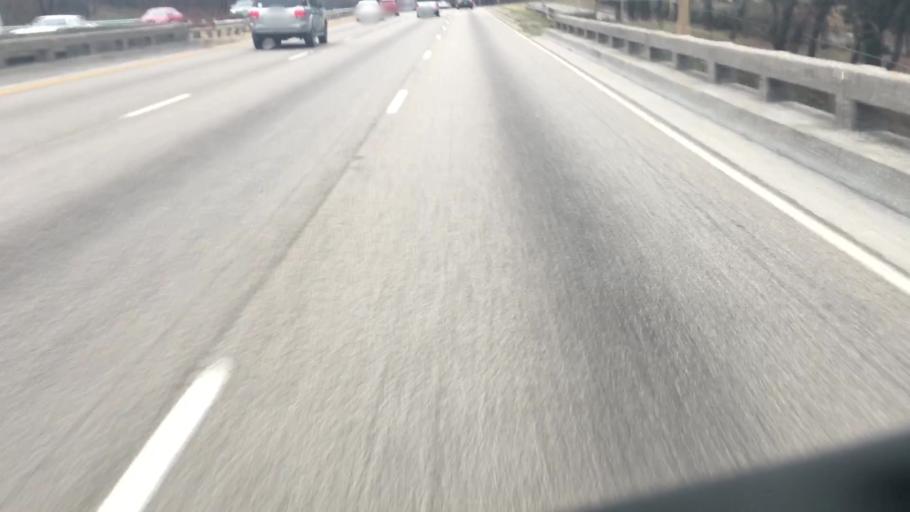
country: US
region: Alabama
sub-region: Jefferson County
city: Homewood
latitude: 33.4918
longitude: -86.7867
